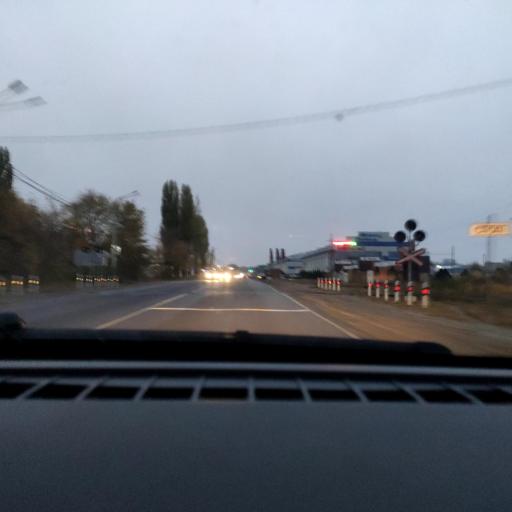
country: RU
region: Voronezj
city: Maslovka
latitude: 51.6411
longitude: 39.2941
